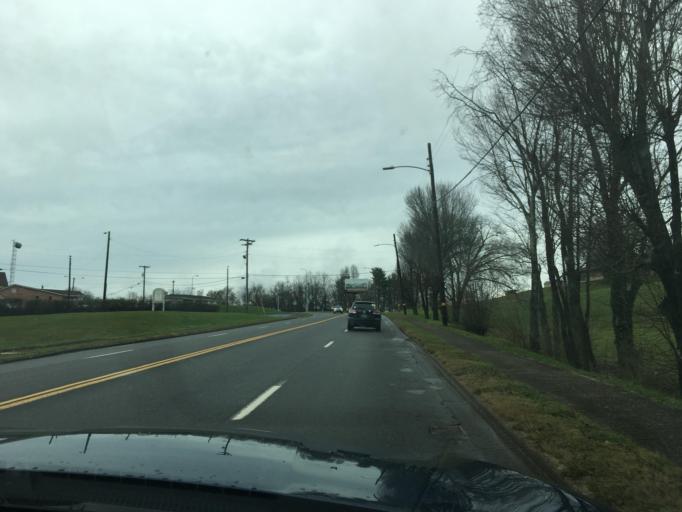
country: US
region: Tennessee
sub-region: McMinn County
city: Athens
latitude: 35.4485
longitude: -84.5949
